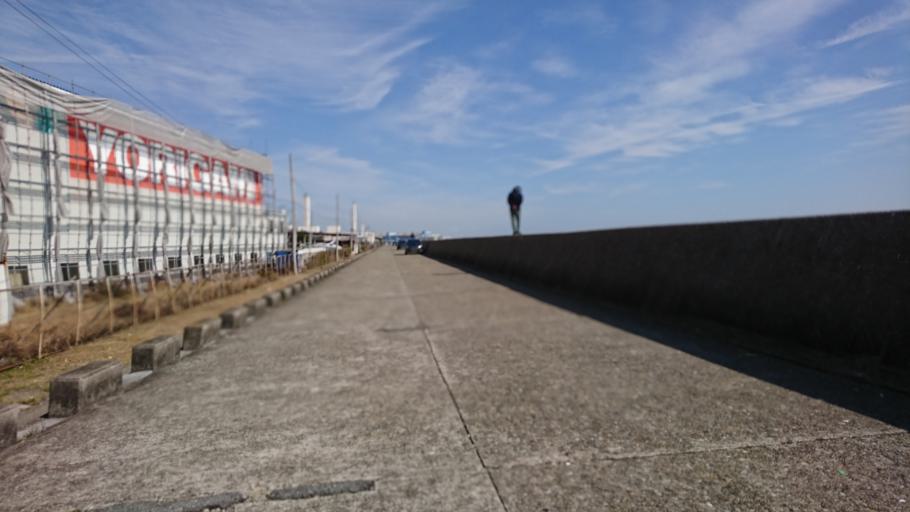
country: JP
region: Hyogo
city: Kakogawacho-honmachi
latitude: 34.6963
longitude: 134.8421
